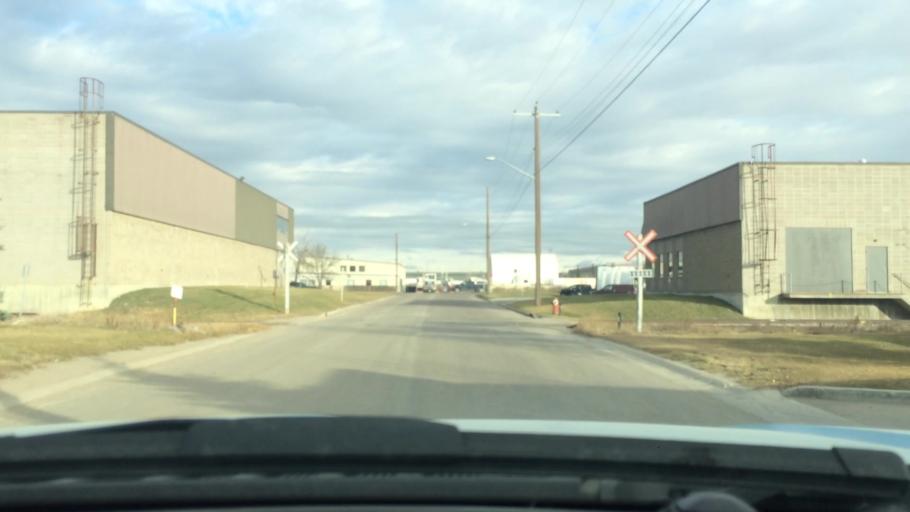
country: CA
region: Alberta
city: Calgary
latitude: 51.0026
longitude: -113.9673
